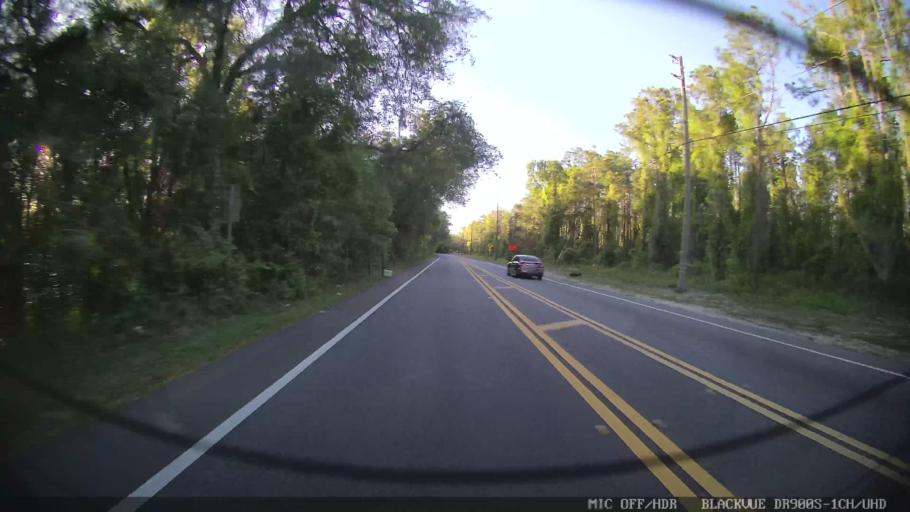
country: US
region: Florida
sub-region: Pasco County
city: Shady Hills
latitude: 28.3322
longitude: -82.5430
